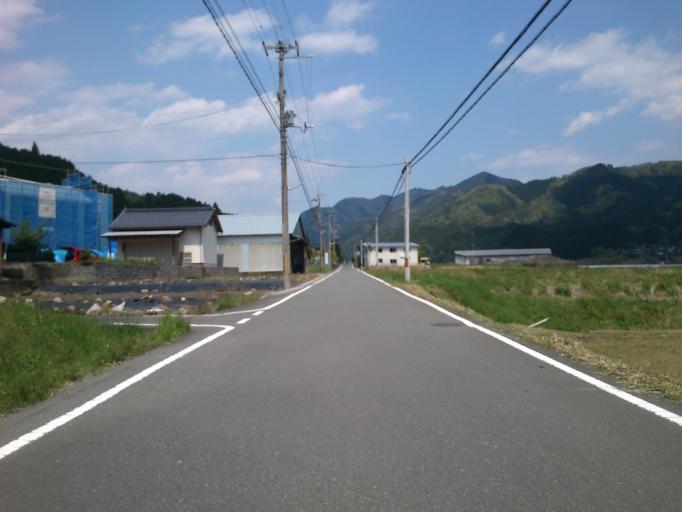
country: JP
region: Kyoto
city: Fukuchiyama
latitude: 35.3522
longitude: 134.9490
